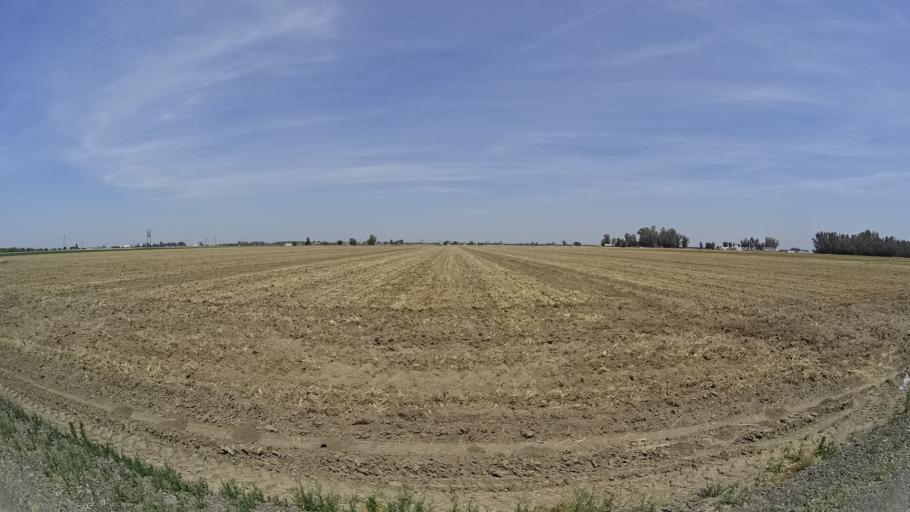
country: US
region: California
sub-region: Fresno County
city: Riverdale
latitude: 36.4019
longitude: -119.8487
